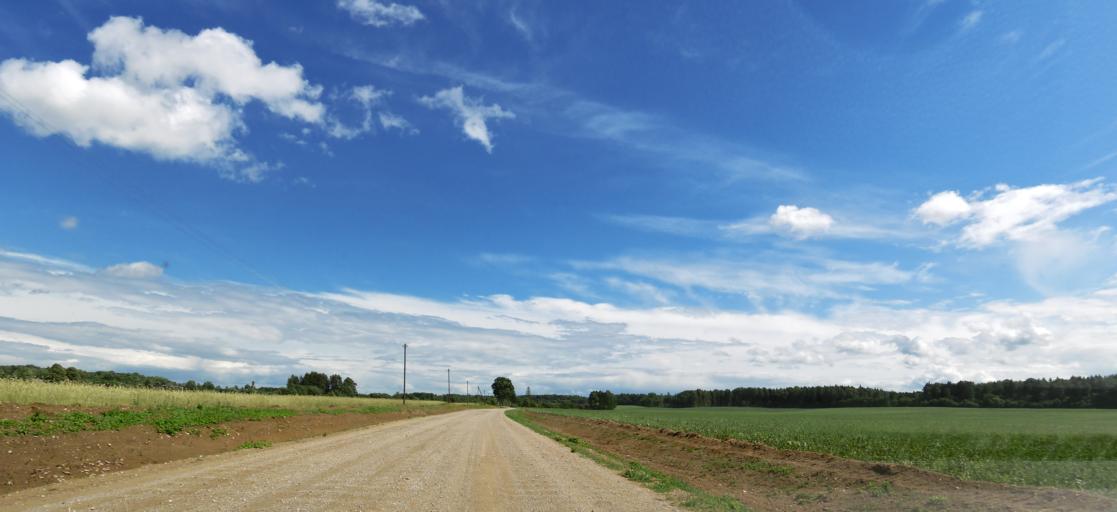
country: LT
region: Panevezys
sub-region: Birzai
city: Birzai
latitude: 56.4126
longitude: 24.8108
